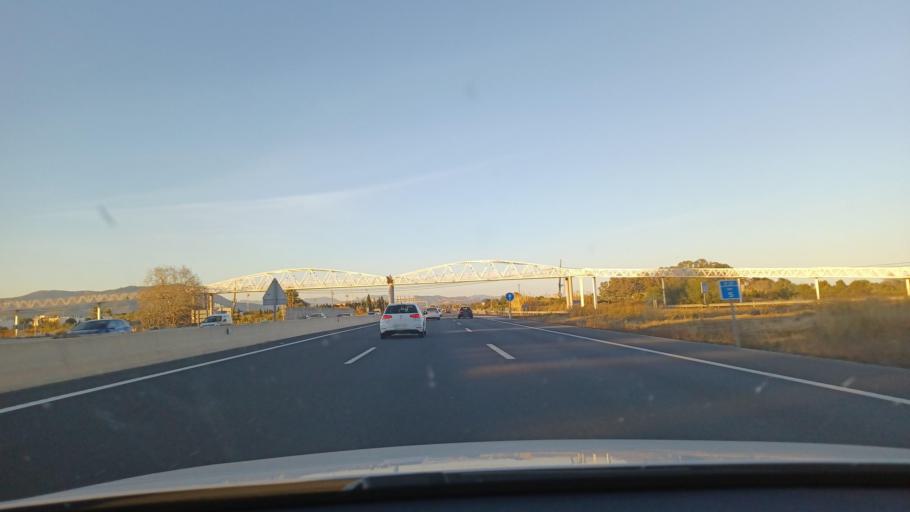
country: ES
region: Valencia
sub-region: Provincia de Valencia
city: Puig
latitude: 39.5867
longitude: -0.2937
